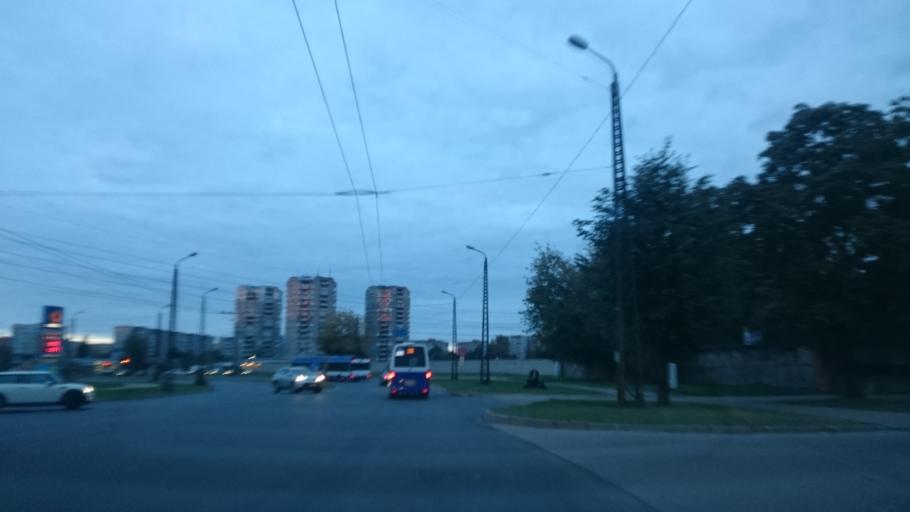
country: LV
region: Stopini
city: Ulbroka
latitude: 56.9305
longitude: 24.1996
